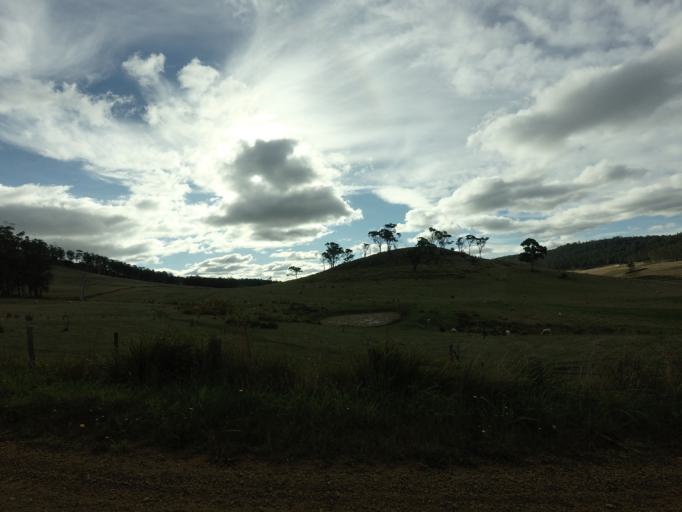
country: AU
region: Tasmania
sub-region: Brighton
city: Bridgewater
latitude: -42.4906
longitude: 147.3260
